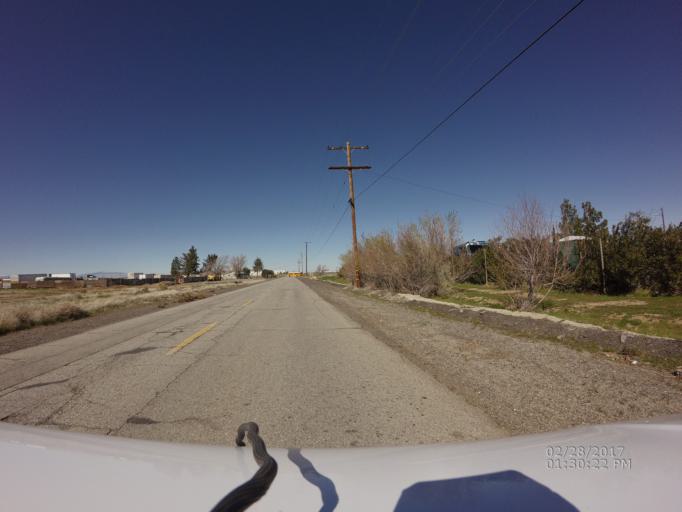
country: US
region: California
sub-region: Los Angeles County
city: Palmdale
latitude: 34.5927
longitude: -118.1164
